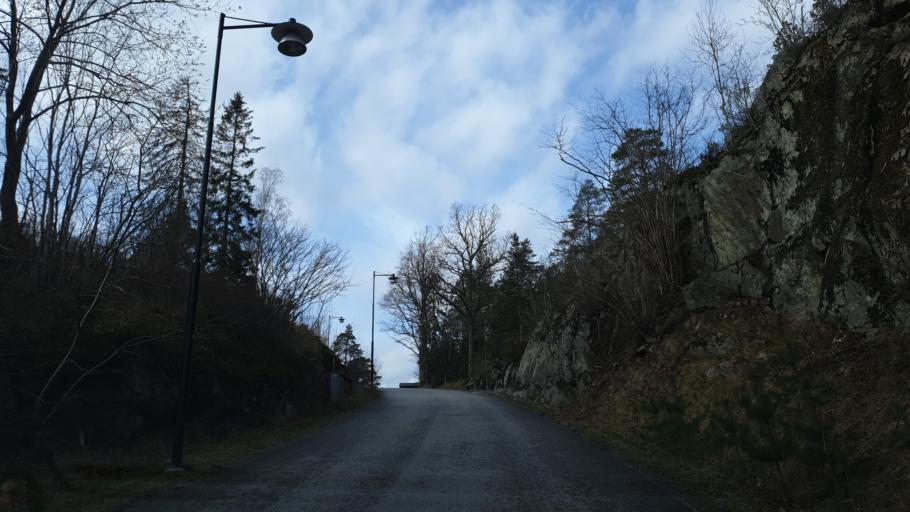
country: SE
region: Stockholm
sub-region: Nacka Kommun
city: Boo
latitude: 59.3311
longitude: 18.2991
